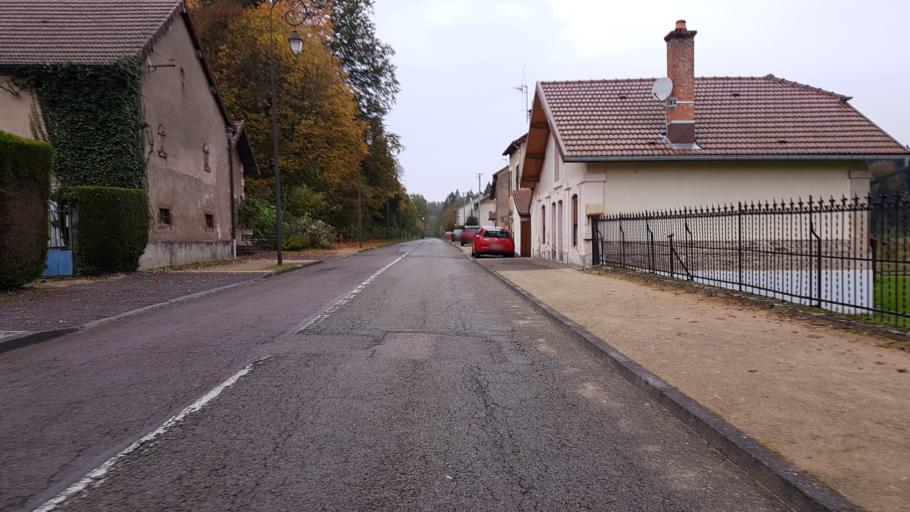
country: FR
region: Franche-Comte
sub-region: Departement de la Haute-Saone
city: Luxeuil-les-Bains
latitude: 47.8238
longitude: 6.3735
